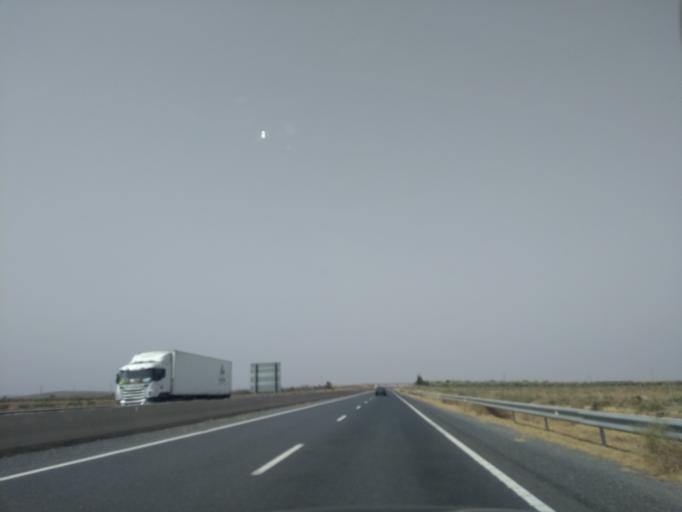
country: MA
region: Marrakech-Tensift-Al Haouz
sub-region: Marrakech
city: Marrakesh
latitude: 31.7638
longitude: -8.1796
